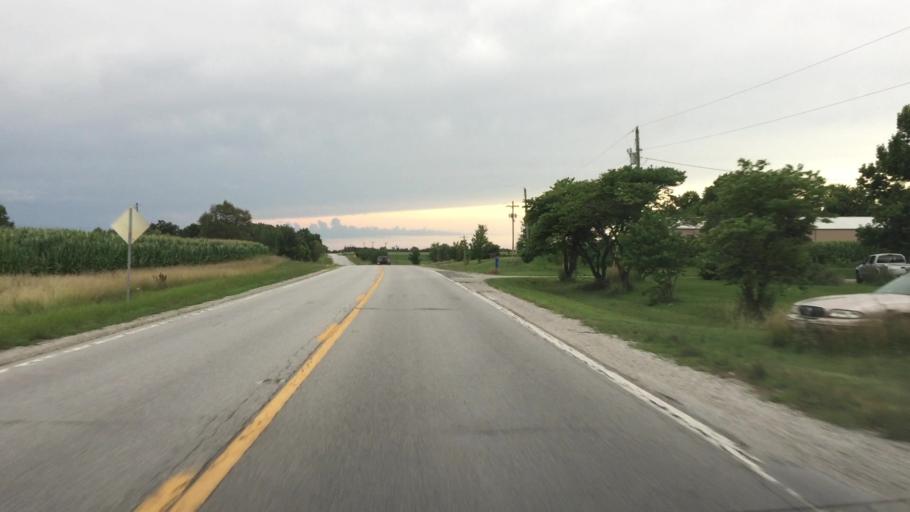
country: US
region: Illinois
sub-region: Hancock County
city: Hamilton
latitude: 40.3768
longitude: -91.3421
